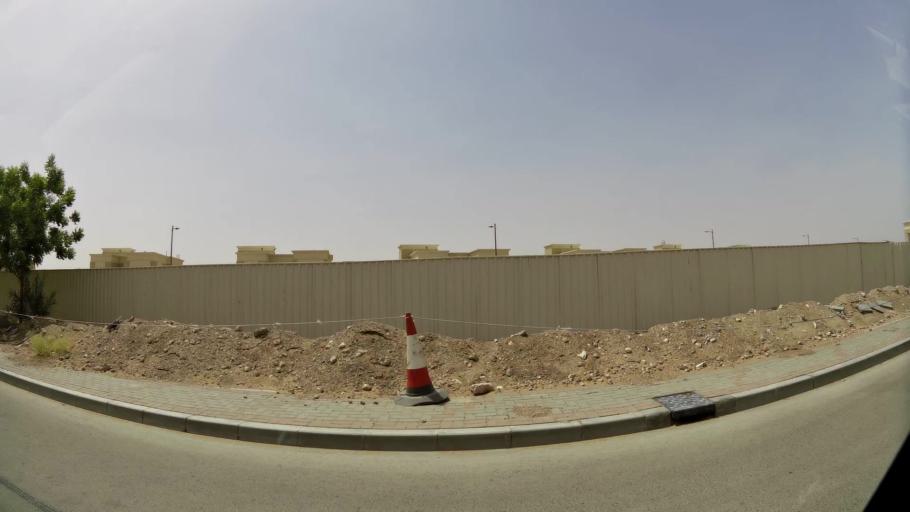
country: AE
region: Abu Dhabi
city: Al Ain
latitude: 24.1430
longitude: 55.6316
